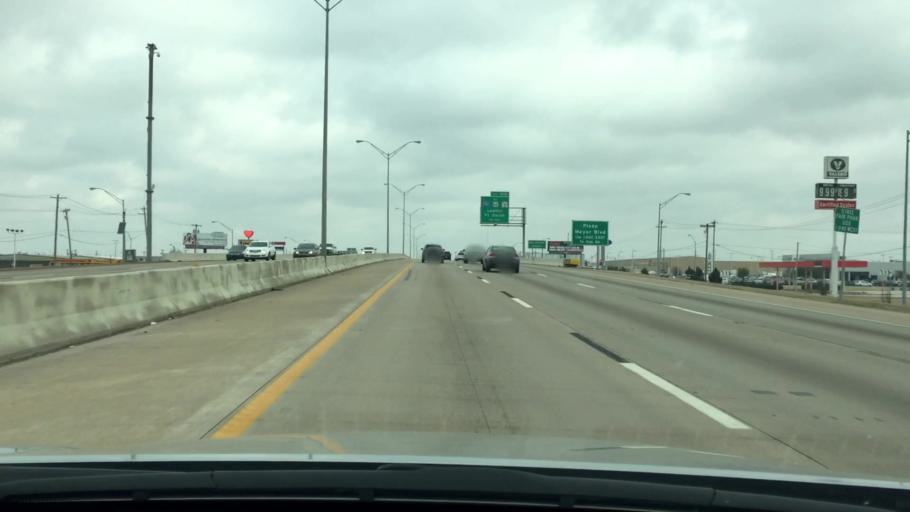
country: US
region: Oklahoma
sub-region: Cleveland County
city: Moore
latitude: 35.3756
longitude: -97.4949
